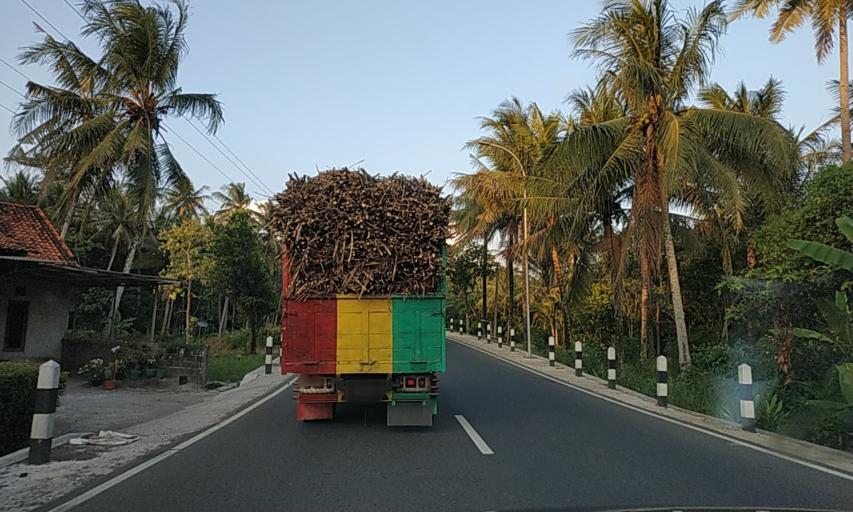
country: ID
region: Central Java
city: Kutoarjo
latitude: -7.8849
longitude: 110.0438
